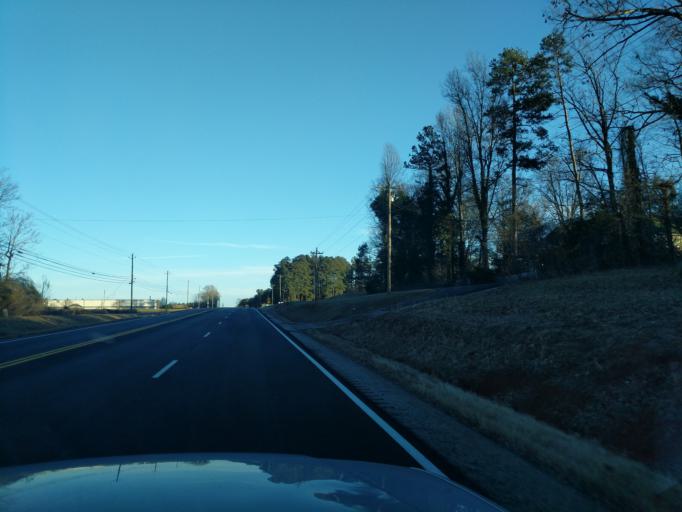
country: US
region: Georgia
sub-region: Stephens County
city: Toccoa
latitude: 34.5167
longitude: -83.2323
